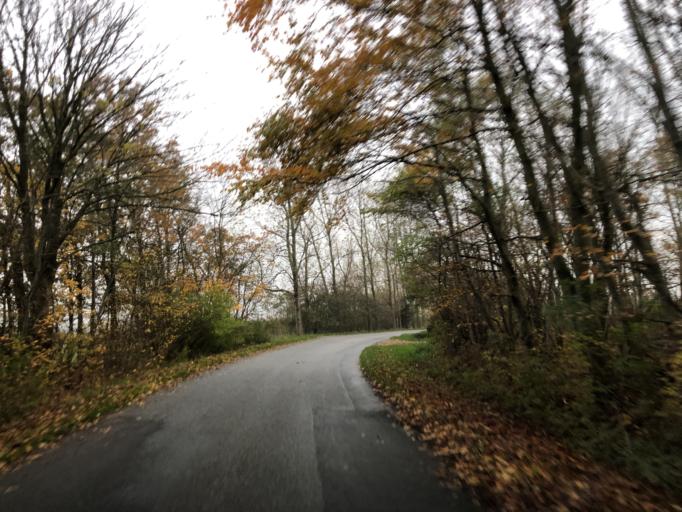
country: DK
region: Central Jutland
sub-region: Herning Kommune
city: Vildbjerg
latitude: 56.2202
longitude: 8.7692
